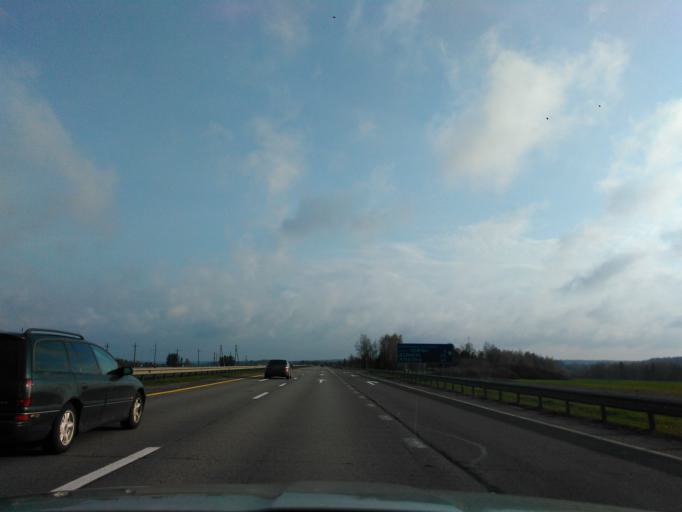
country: BY
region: Minsk
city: Lahoysk
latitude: 54.1625
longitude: 27.8152
